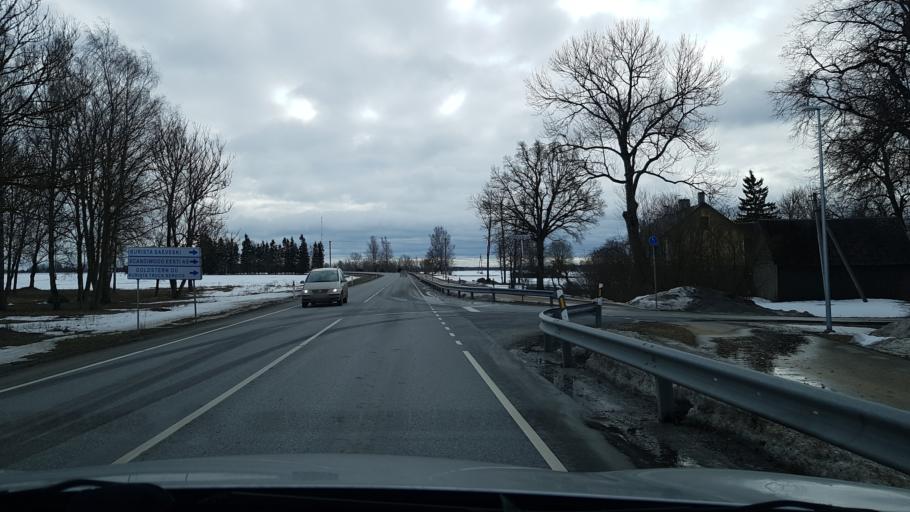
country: EE
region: Jogevamaa
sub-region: Jogeva linn
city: Jogeva
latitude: 58.7592
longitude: 26.3351
